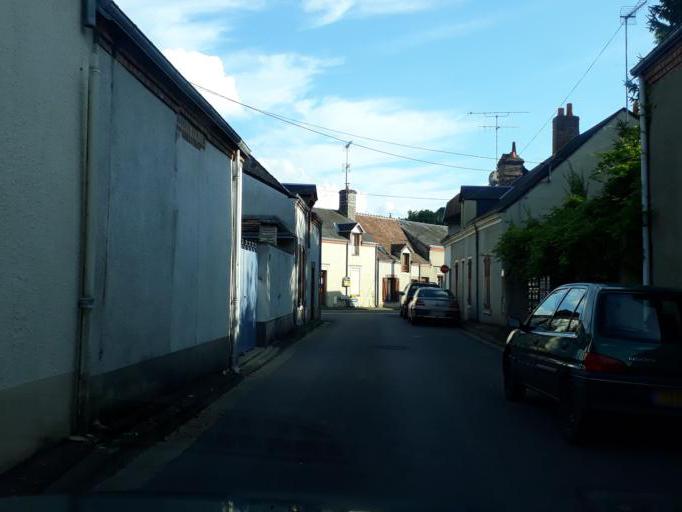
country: FR
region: Centre
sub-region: Departement du Loir-et-Cher
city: Moree
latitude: 47.9019
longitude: 1.2344
